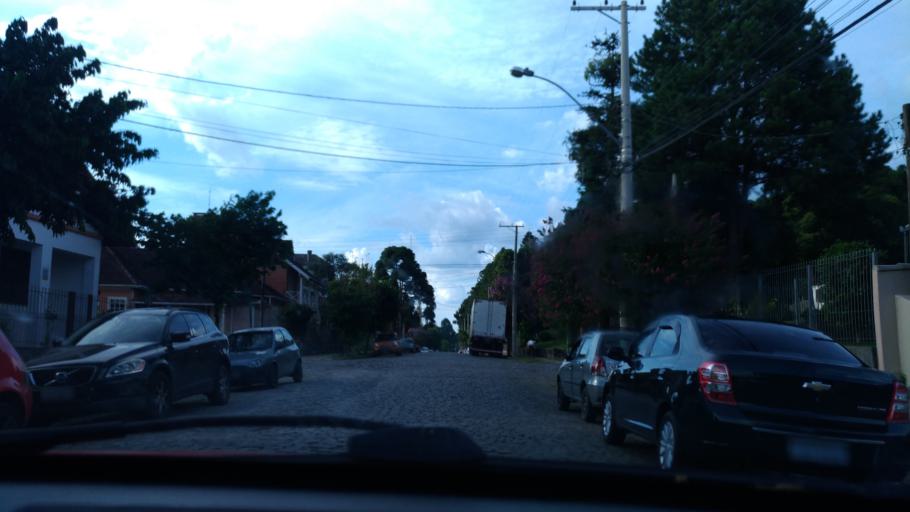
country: BR
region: Rio Grande do Sul
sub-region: Canela
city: Canela
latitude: -29.3578
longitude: -50.8129
